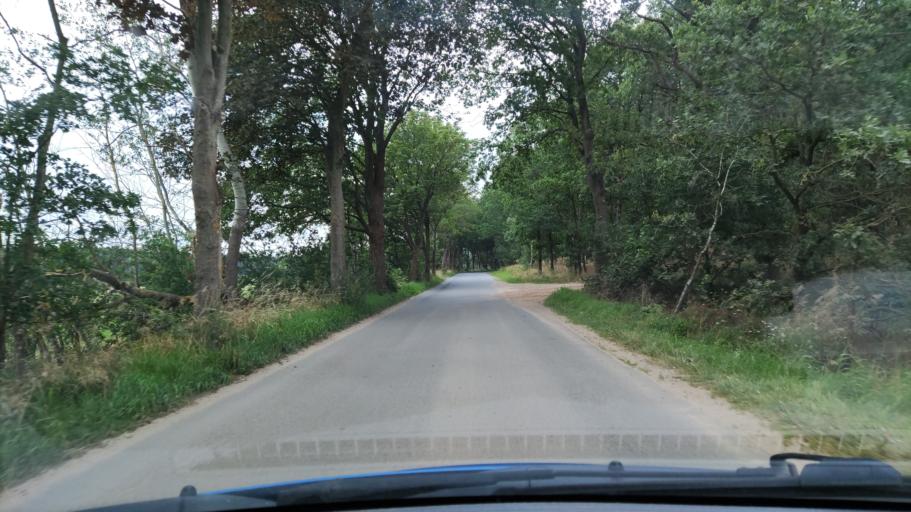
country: DE
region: Lower Saxony
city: Stoetze
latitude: 53.0301
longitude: 10.7648
